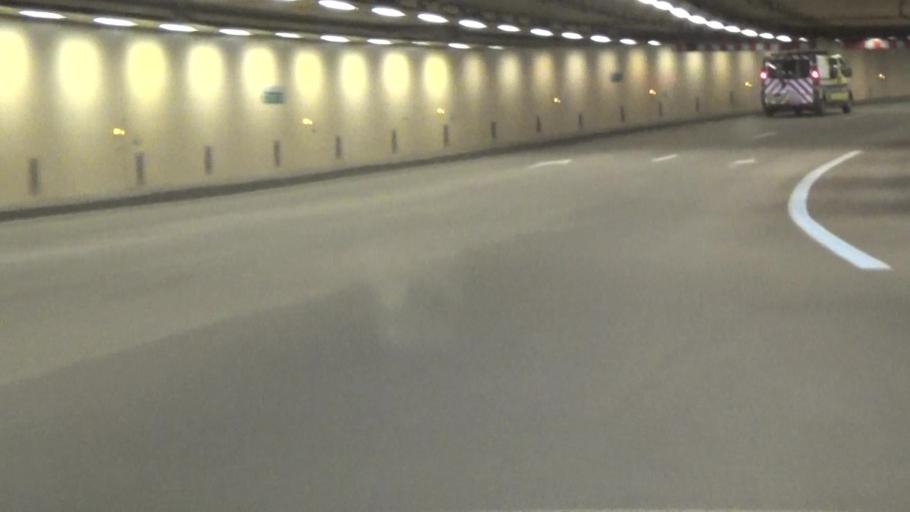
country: FR
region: Ile-de-France
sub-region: Departement des Yvelines
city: Bougival
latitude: 48.8692
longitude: 2.1588
